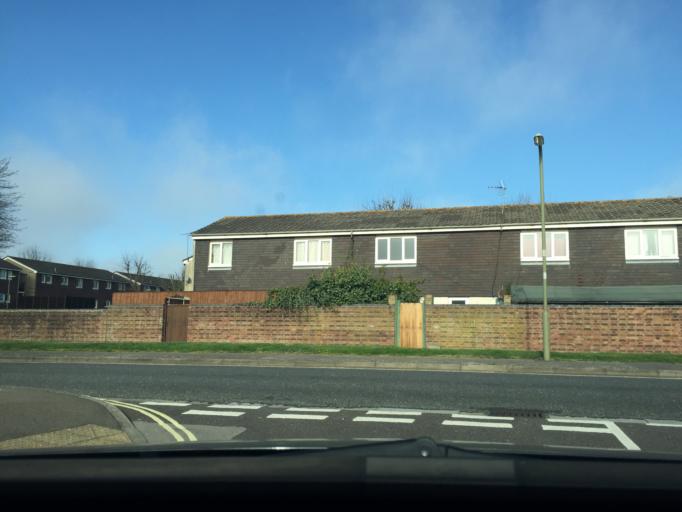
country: GB
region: England
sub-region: Hampshire
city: Gosport
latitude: 50.8079
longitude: -1.1356
